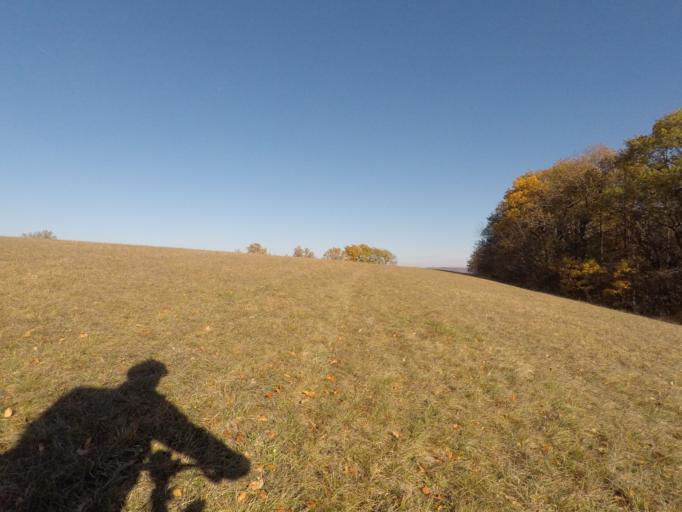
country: DE
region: Baden-Wuerttemberg
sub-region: Tuebingen Region
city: Pfullingen
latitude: 48.4454
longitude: 9.2264
